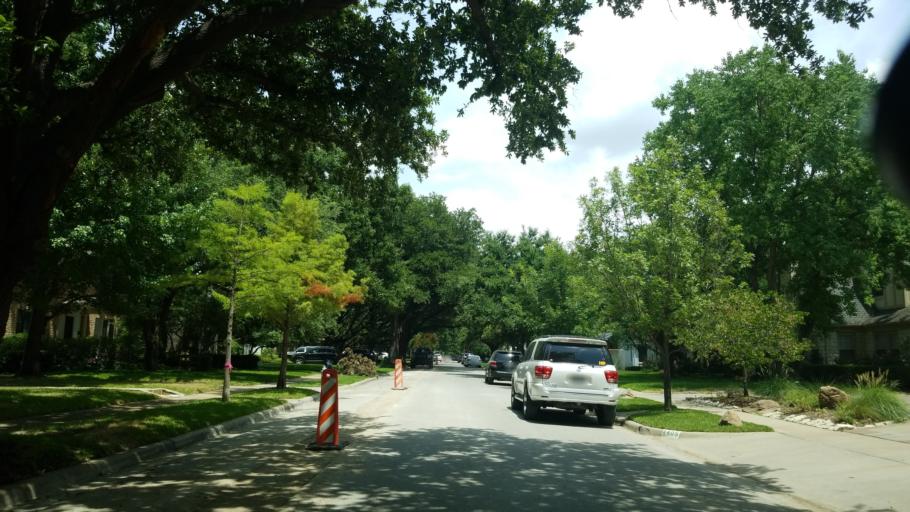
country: US
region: Texas
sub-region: Dallas County
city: University Park
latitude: 32.8531
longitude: -96.8111
